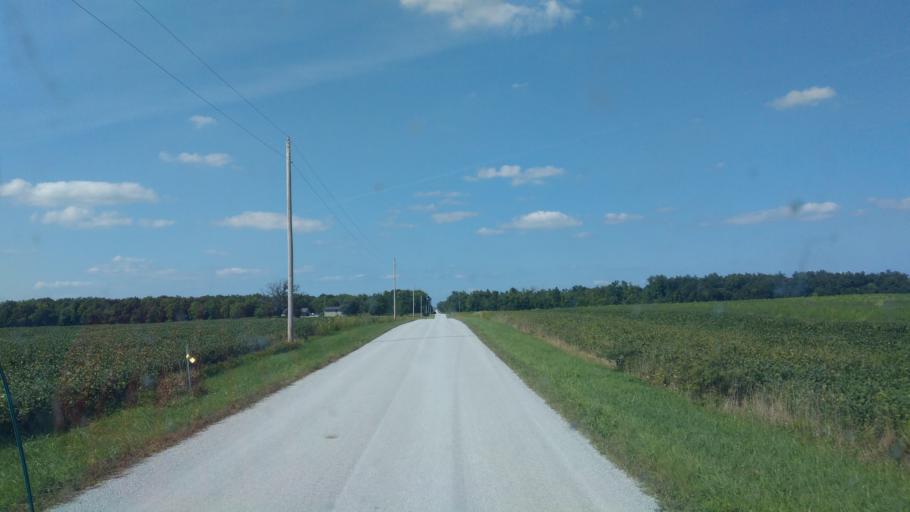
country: US
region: Ohio
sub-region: Hardin County
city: Kenton
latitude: 40.6464
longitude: -83.4390
